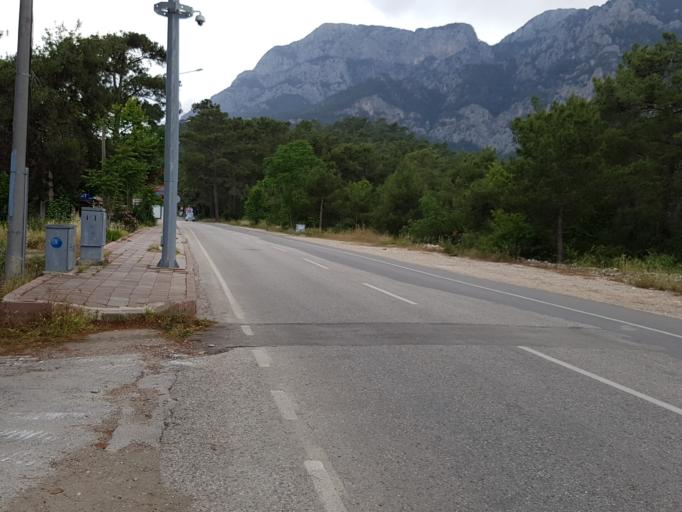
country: TR
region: Antalya
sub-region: Kemer
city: Goeynuek
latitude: 36.6461
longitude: 30.5497
